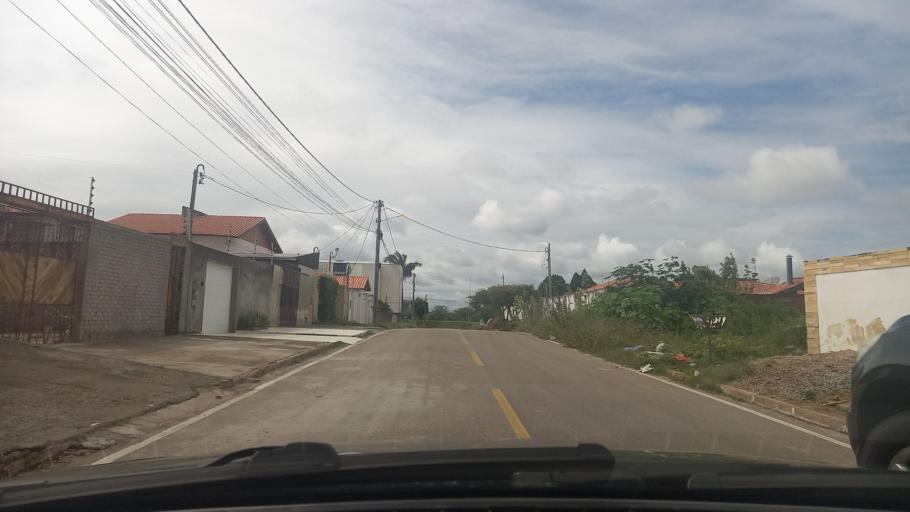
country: BR
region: Bahia
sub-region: Paulo Afonso
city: Paulo Afonso
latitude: -9.3995
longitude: -38.2448
